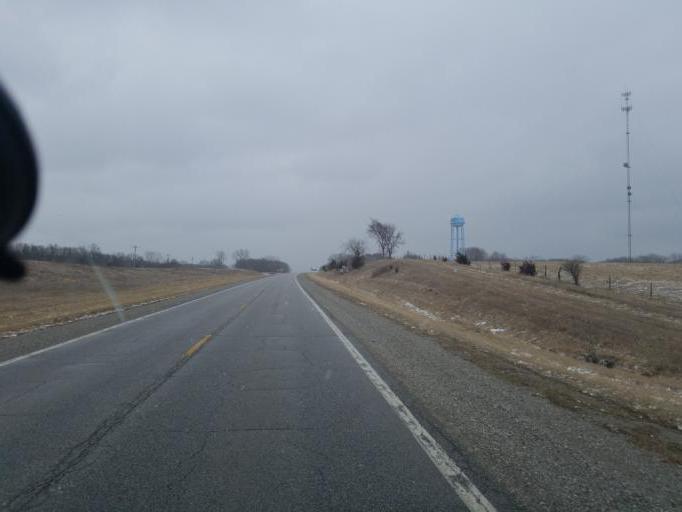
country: US
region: Missouri
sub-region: Putnam County
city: Unionville
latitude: 40.4710
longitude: -92.8157
